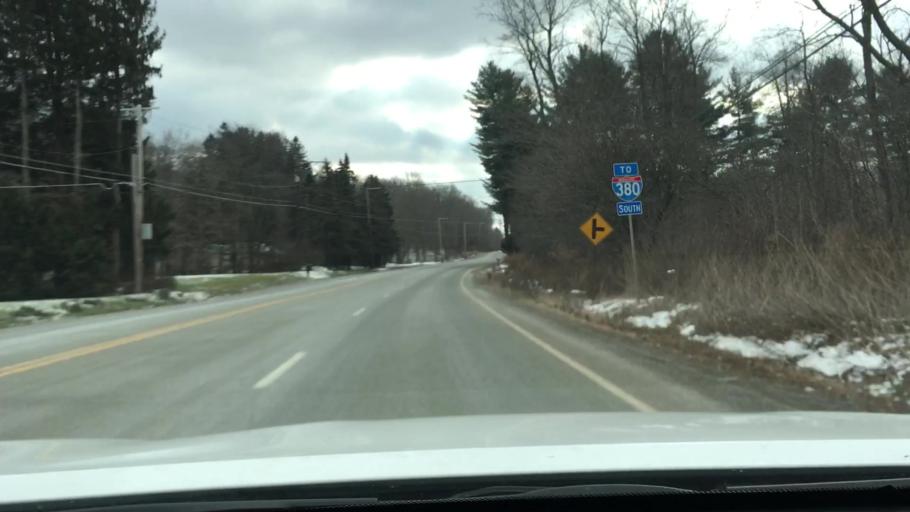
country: US
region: Pennsylvania
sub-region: Lackawanna County
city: Moscow
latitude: 41.2451
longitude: -75.5018
